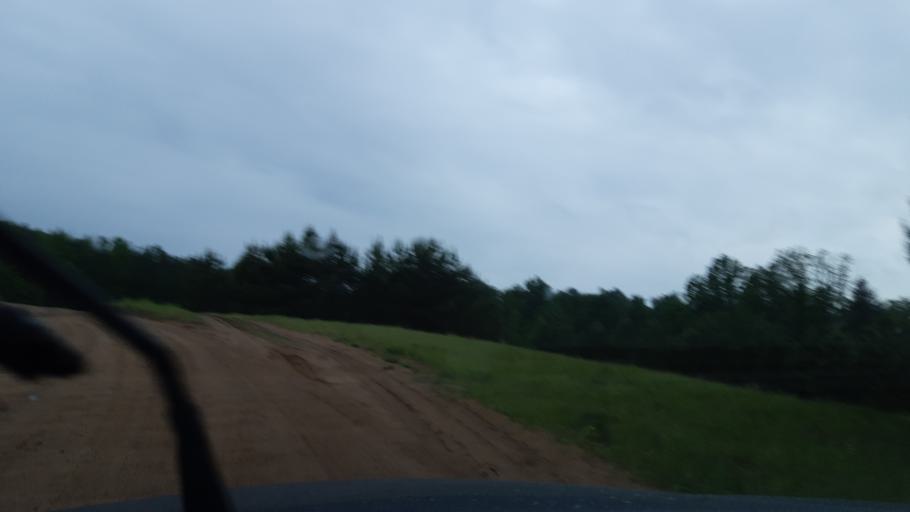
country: LT
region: Utenos apskritis
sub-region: Anyksciai
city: Anyksciai
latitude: 55.4518
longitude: 25.2127
